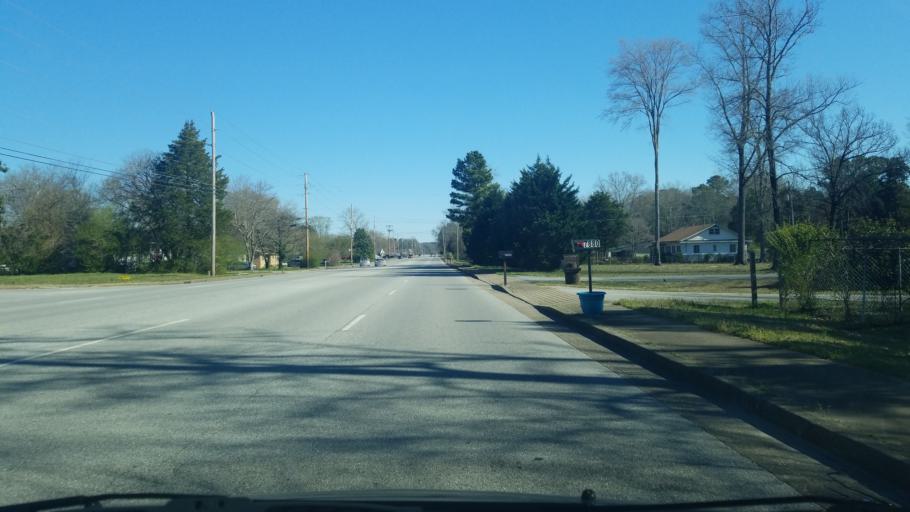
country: US
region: Tennessee
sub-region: Hamilton County
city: Middle Valley
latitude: 35.1827
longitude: -85.1694
